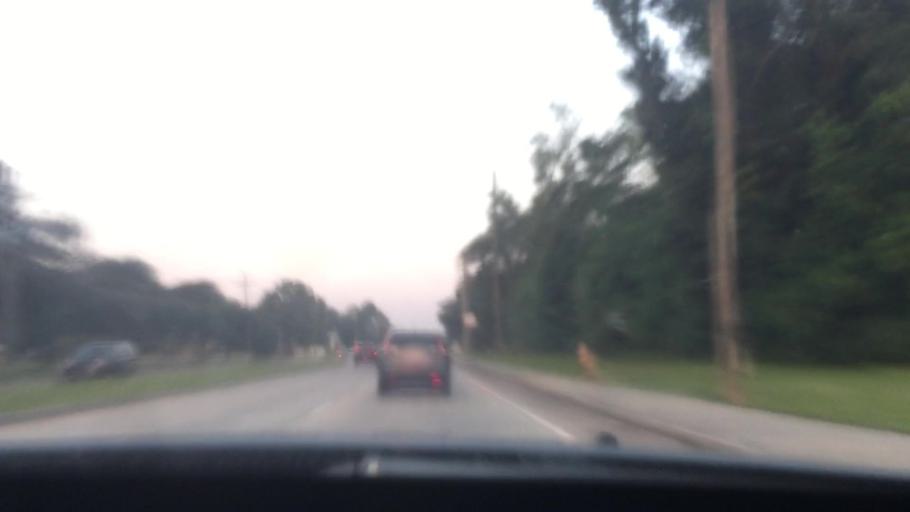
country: US
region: Louisiana
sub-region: East Baton Rouge Parish
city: Shenandoah
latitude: 30.4285
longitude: -91.0204
